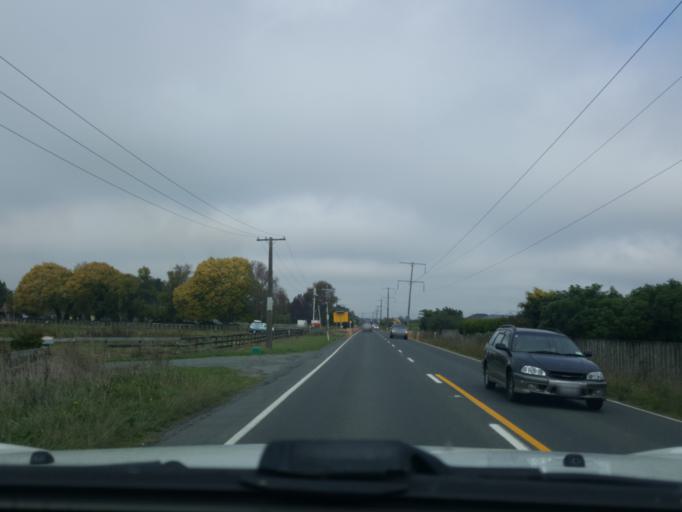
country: NZ
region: Waikato
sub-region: Hamilton City
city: Hamilton
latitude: -37.7341
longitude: 175.2877
